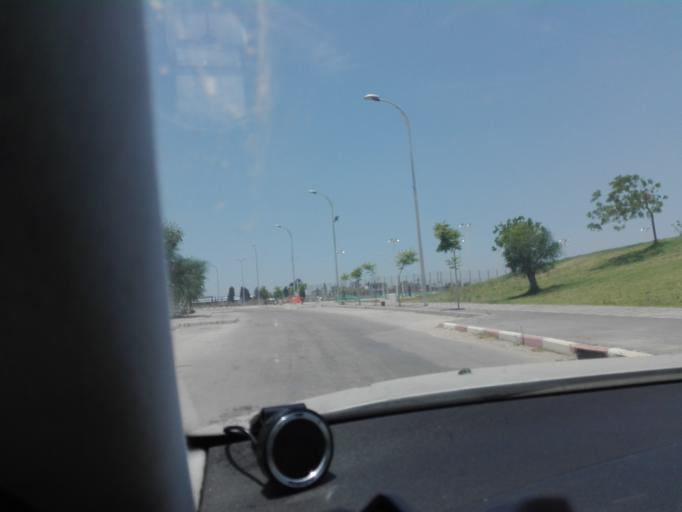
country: IL
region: Central District
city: Bene 'Ayish
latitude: 31.7414
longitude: 34.7438
